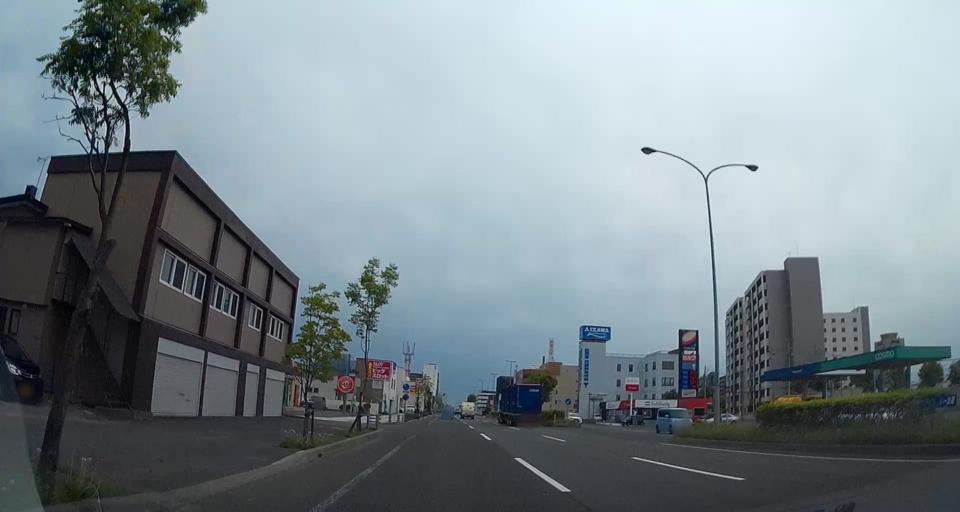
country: JP
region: Hokkaido
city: Tomakomai
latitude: 42.6365
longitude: 141.6076
